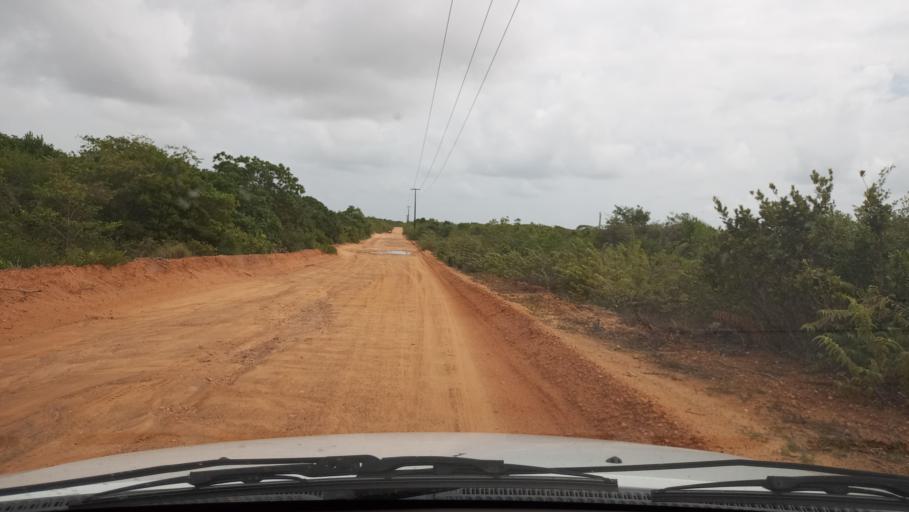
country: BR
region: Rio Grande do Norte
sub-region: Maxaranguape
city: Sao Miguel
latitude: -5.4782
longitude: -35.3024
